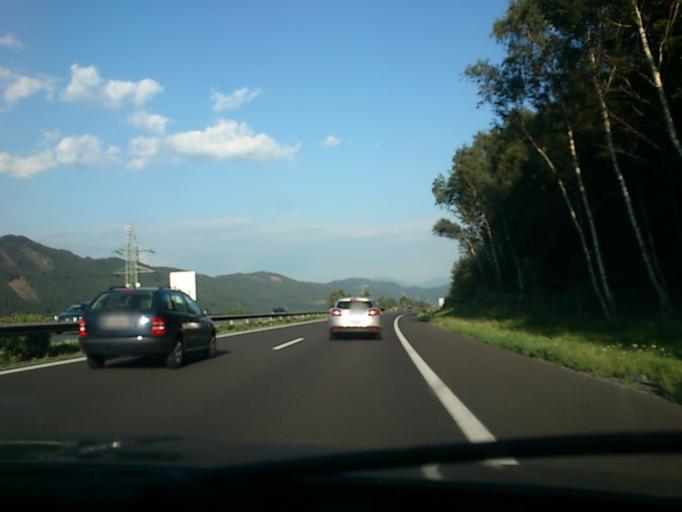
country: AT
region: Styria
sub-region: Politischer Bezirk Leoben
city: Kammern im Liesingtal
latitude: 47.3873
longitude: 14.9122
